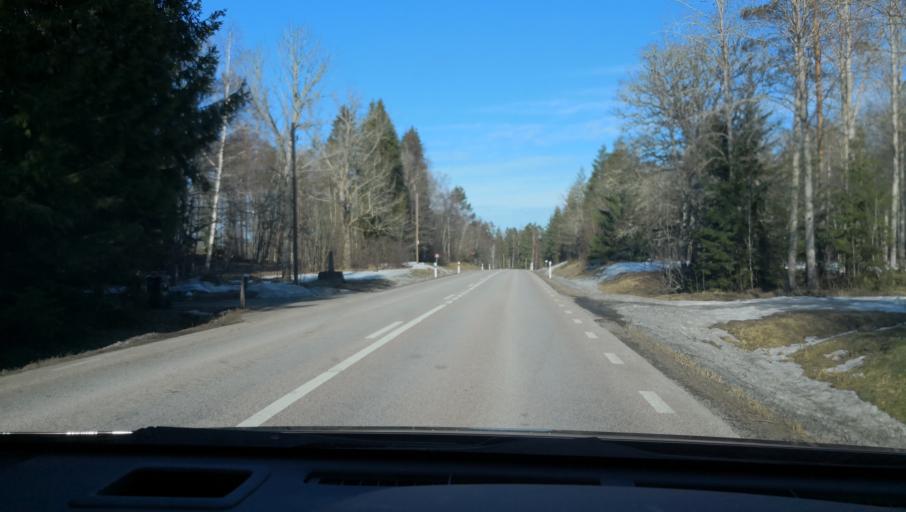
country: SE
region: Uppsala
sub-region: Osthammars Kommun
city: Osterbybruk
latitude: 60.1584
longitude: 17.8372
